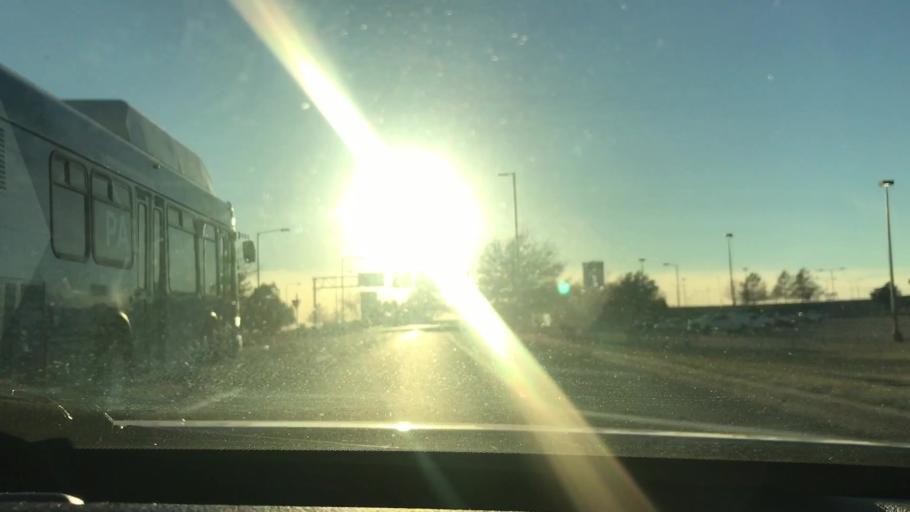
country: US
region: Missouri
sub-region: Platte County
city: Weatherby Lake
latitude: 39.2999
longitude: -94.7165
